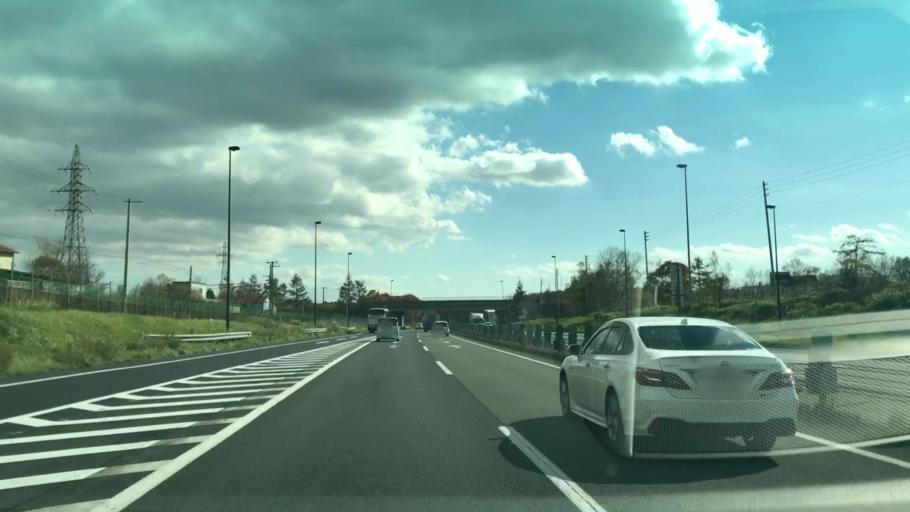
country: JP
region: Hokkaido
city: Kitahiroshima
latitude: 42.9498
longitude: 141.5140
